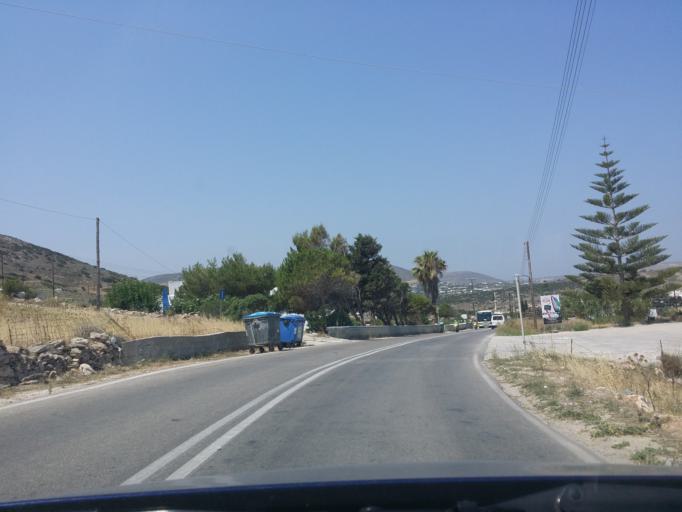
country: GR
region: South Aegean
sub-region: Nomos Kykladon
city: Naousa
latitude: 37.1172
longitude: 25.2419
